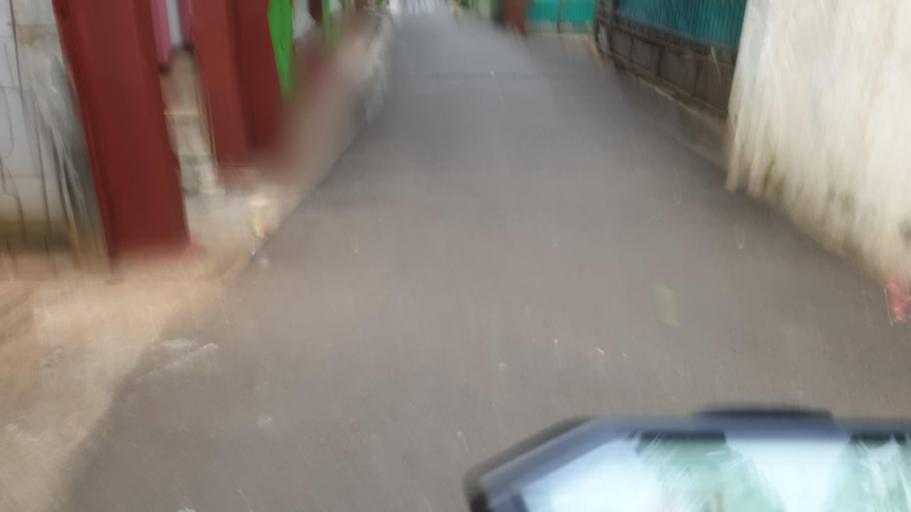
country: ID
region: West Java
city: Depok
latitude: -6.3667
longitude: 106.8380
